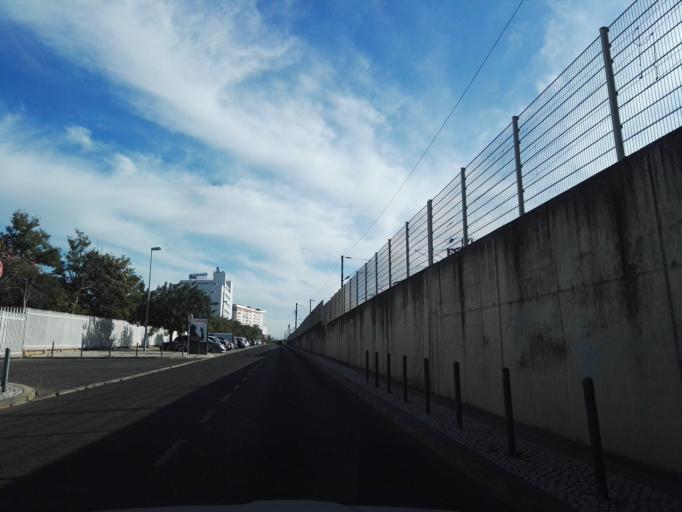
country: PT
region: Lisbon
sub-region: Loures
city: Moscavide
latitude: 38.7607
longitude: -9.0998
